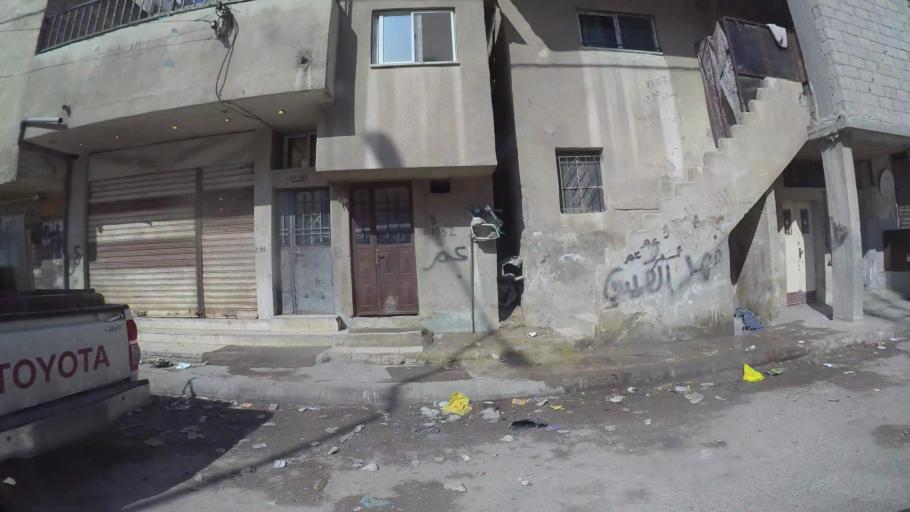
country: JO
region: Amman
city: Al Jubayhah
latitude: 32.0729
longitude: 35.8443
